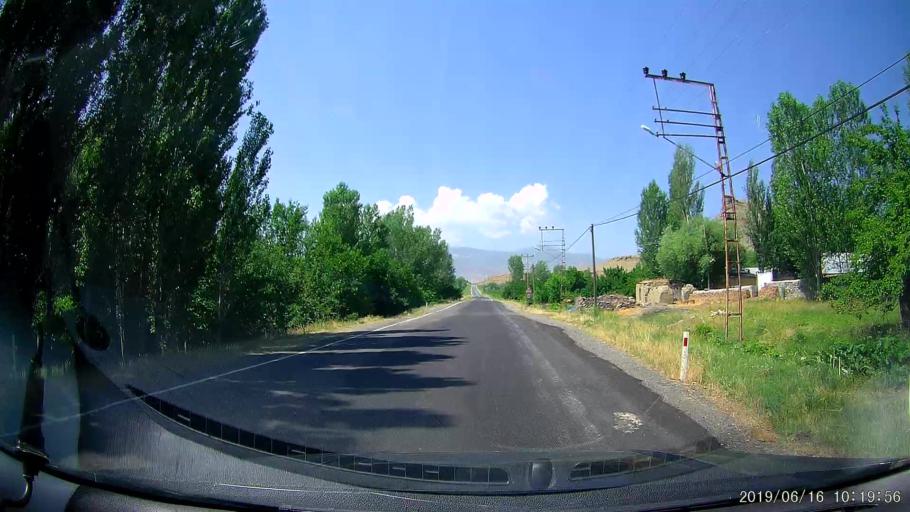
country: TR
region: Igdir
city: Tuzluca
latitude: 40.1518
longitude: 43.6523
